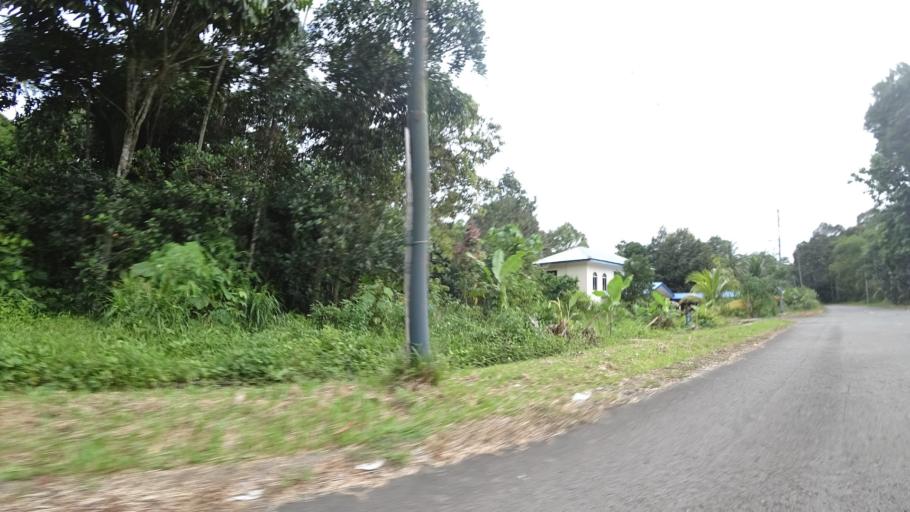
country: MY
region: Sarawak
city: Limbang
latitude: 4.8140
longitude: 114.9434
